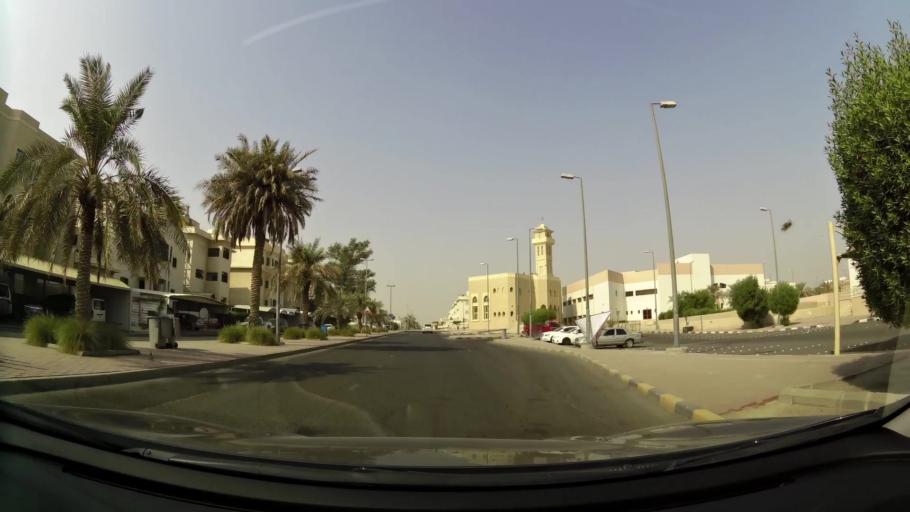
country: KW
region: Al Asimah
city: Ar Rabiyah
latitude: 29.2689
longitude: 47.8752
